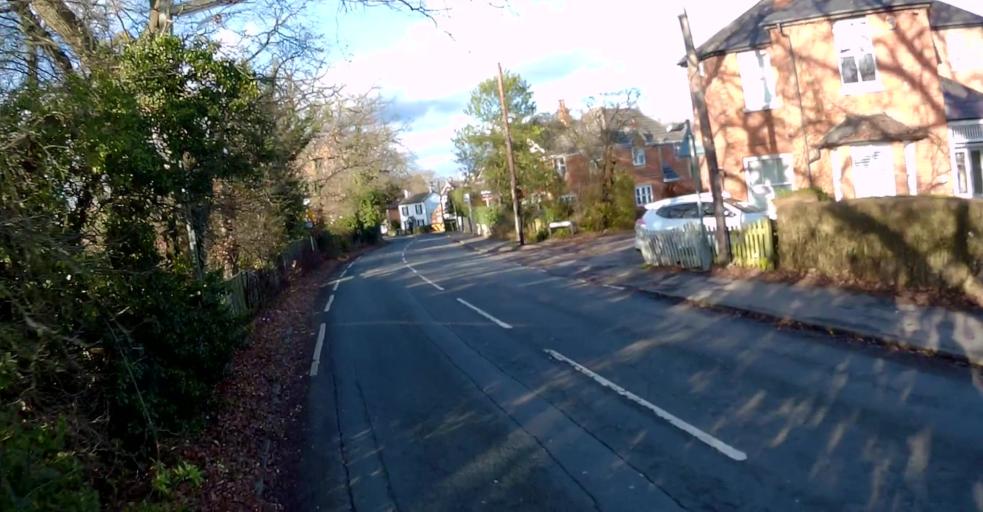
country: GB
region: England
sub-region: Surrey
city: Ottershaw
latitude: 51.3639
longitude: -0.5138
